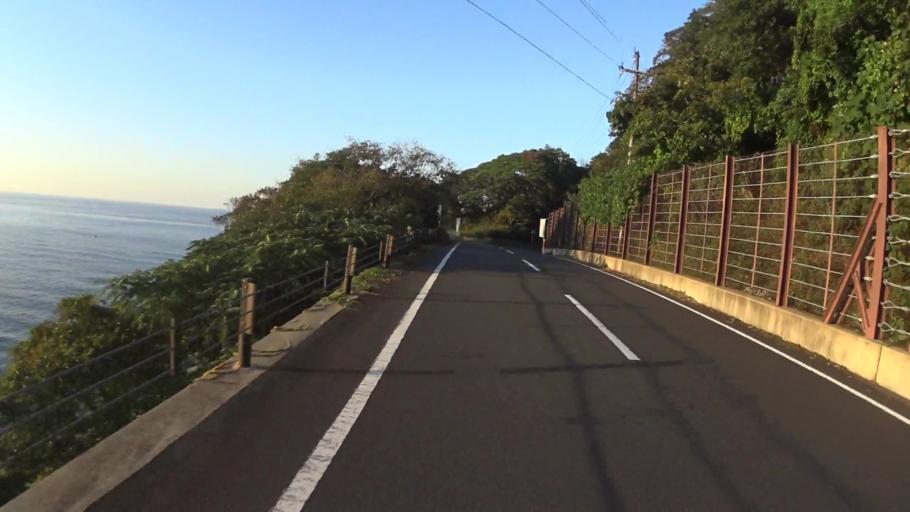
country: JP
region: Hyogo
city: Toyooka
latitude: 35.6912
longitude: 135.0024
